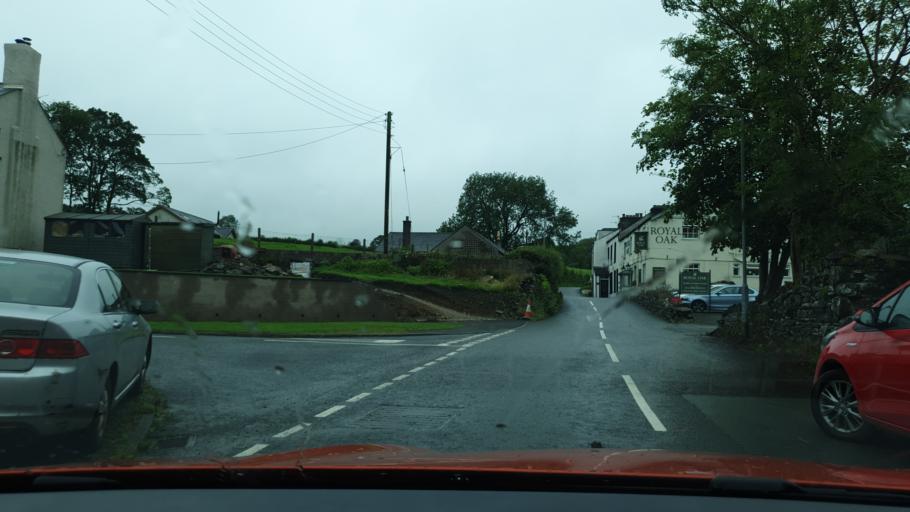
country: GB
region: England
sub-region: Cumbria
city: Ulverston
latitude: 54.2551
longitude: -3.0667
